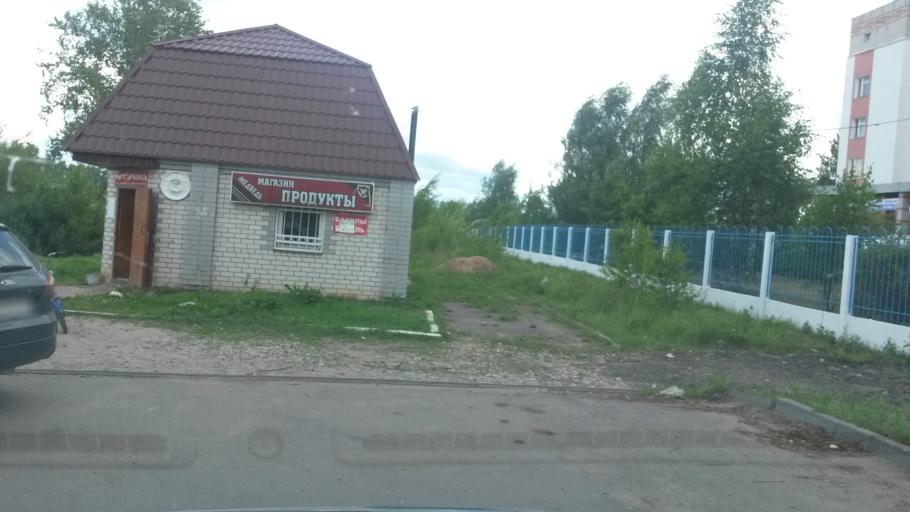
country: RU
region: Jaroslavl
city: Gavrilov-Yam
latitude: 57.3120
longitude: 39.8661
